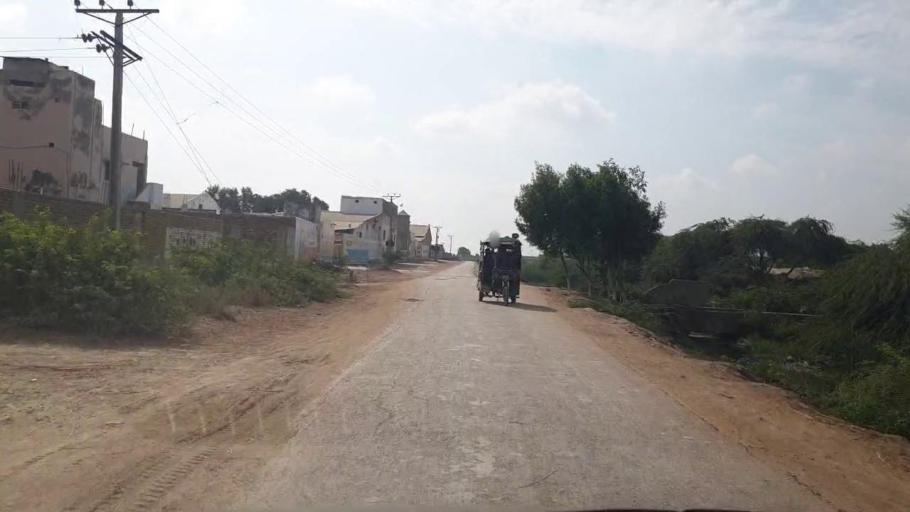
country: PK
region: Sindh
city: Kario
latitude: 24.6495
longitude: 68.5423
